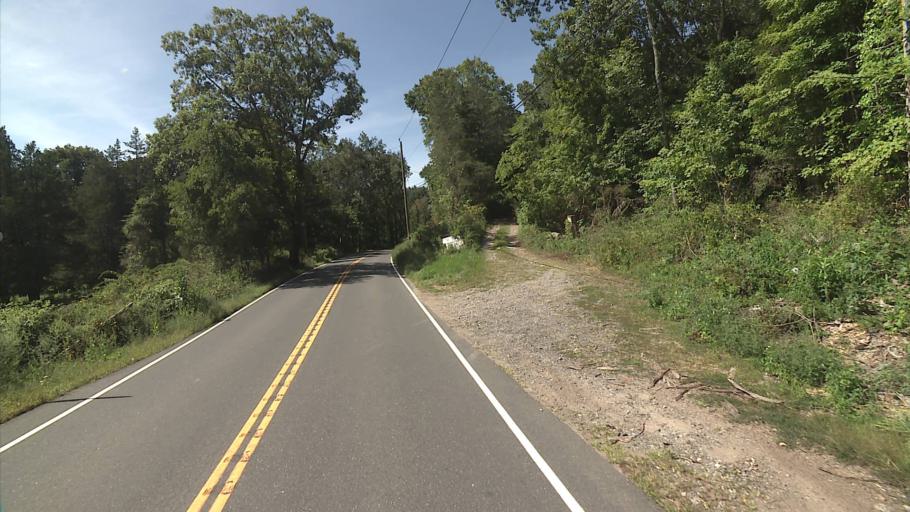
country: US
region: Connecticut
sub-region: New Haven County
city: Oxford
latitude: 41.4468
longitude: -73.1583
